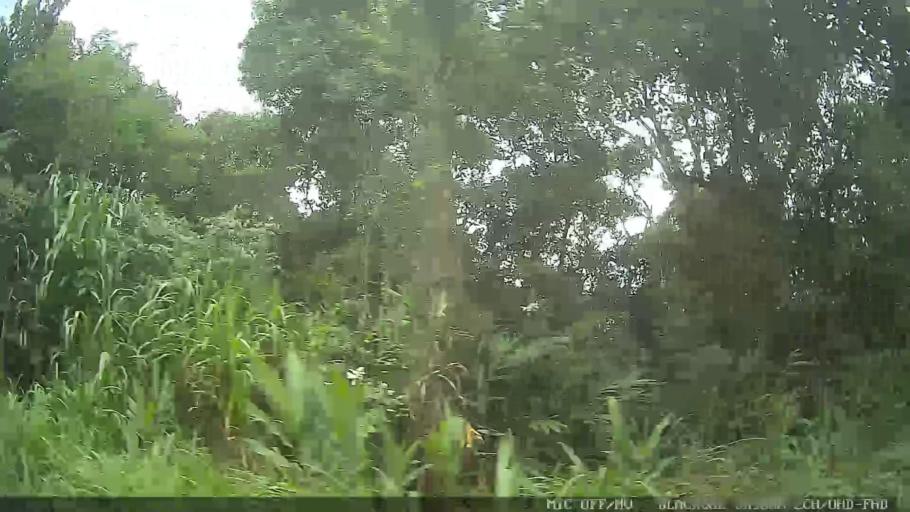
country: BR
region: Sao Paulo
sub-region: Maua
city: Maua
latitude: -23.6241
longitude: -46.3881
